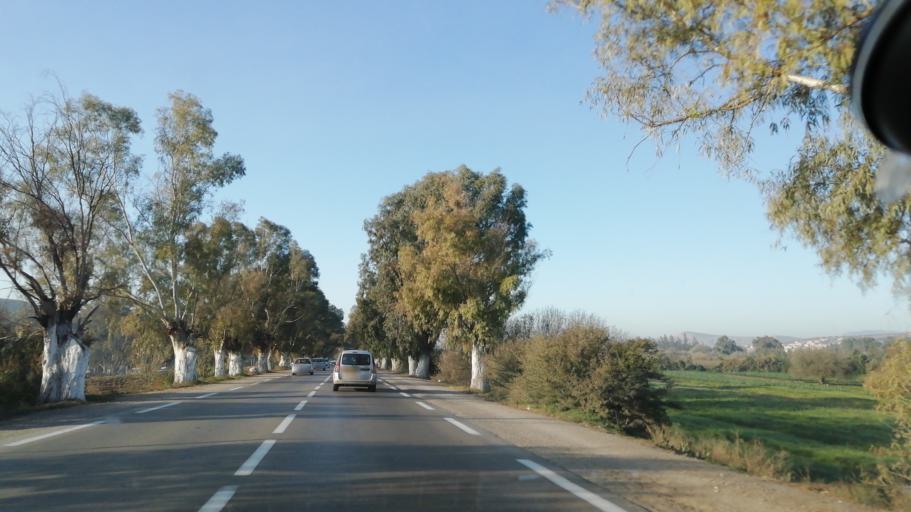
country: DZ
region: Tlemcen
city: Remchi
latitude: 35.0746
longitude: -1.4543
